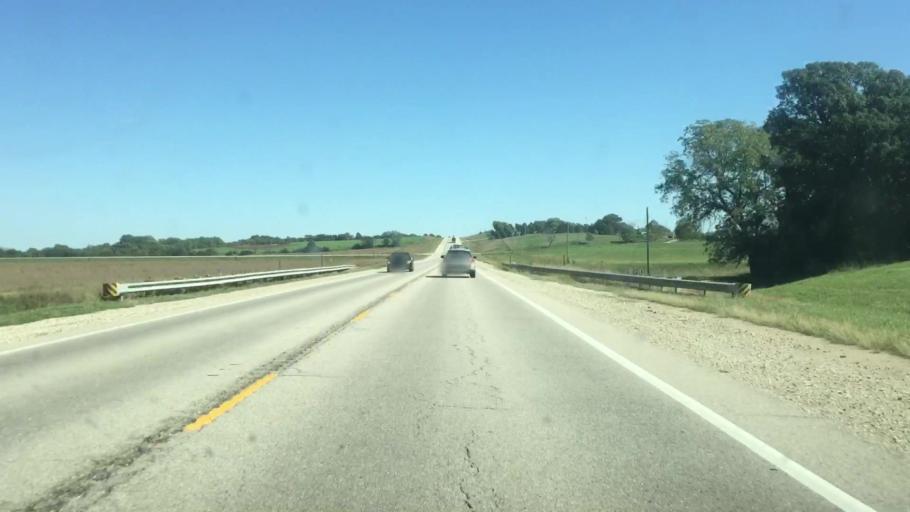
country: US
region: Kansas
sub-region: Nemaha County
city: Seneca
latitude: 39.8431
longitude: -96.0018
